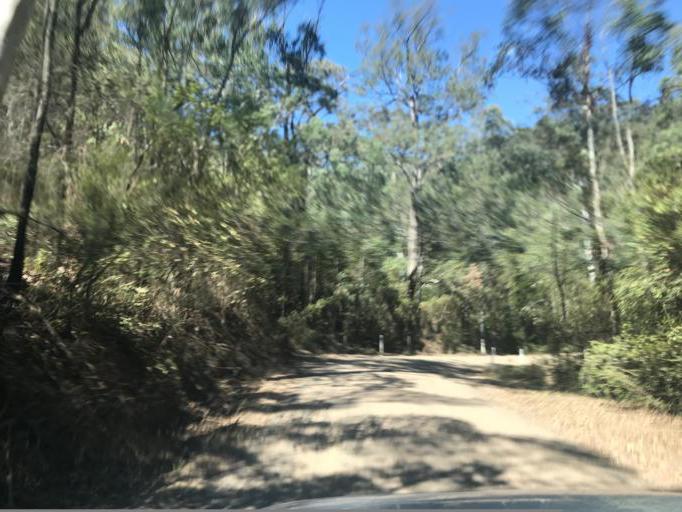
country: AU
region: New South Wales
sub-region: Wyong Shire
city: Little Jilliby
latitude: -33.1862
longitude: 151.0550
